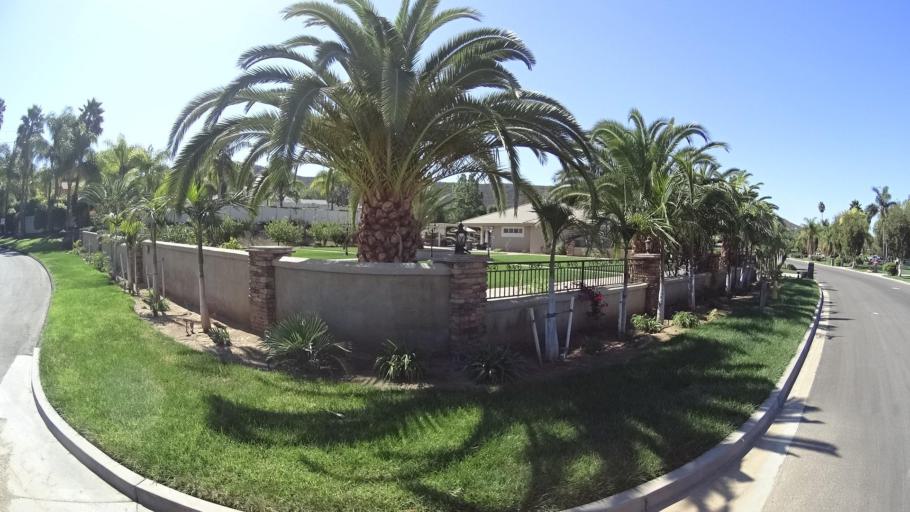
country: US
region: California
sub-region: San Diego County
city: Rancho San Diego
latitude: 32.7396
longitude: -116.9162
